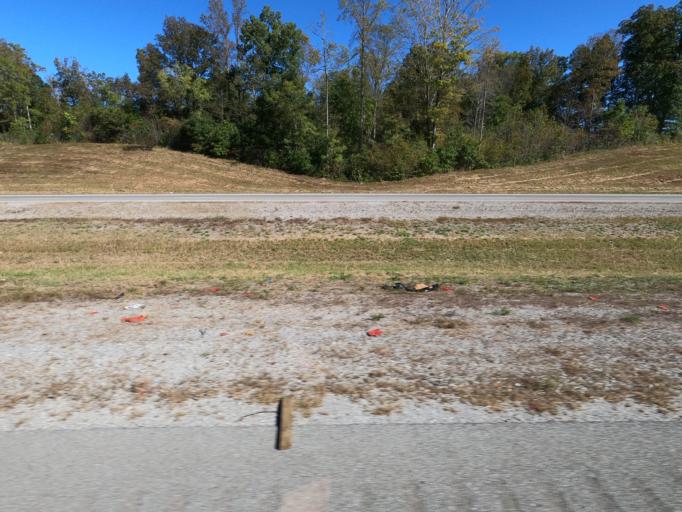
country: US
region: Tennessee
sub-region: Williamson County
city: Fairview
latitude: 35.8577
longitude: -87.0793
